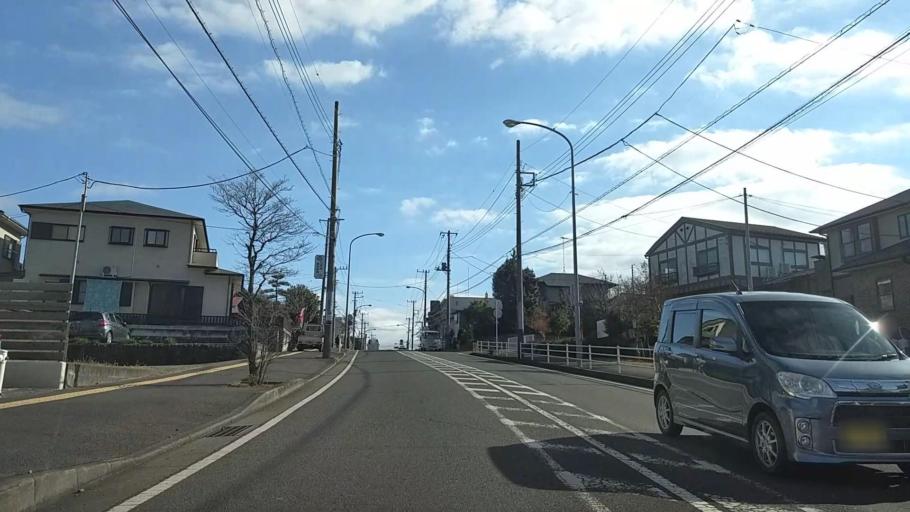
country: JP
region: Kanagawa
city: Isehara
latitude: 35.4003
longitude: 139.3150
